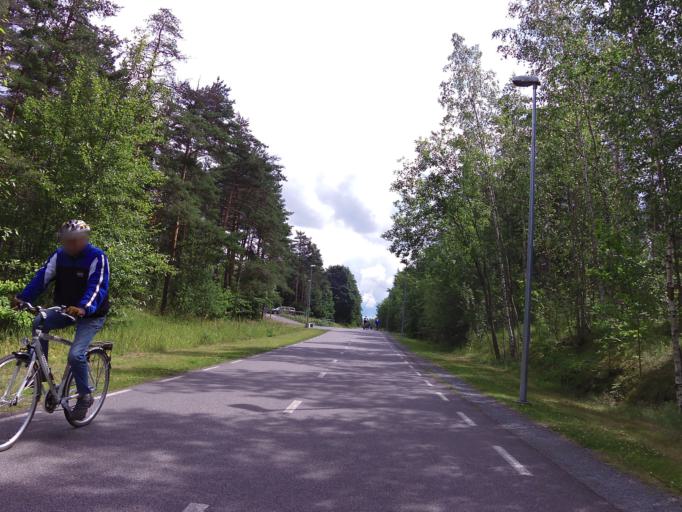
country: EE
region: Harju
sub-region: Saue vald
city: Laagri
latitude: 59.3838
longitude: 24.6470
